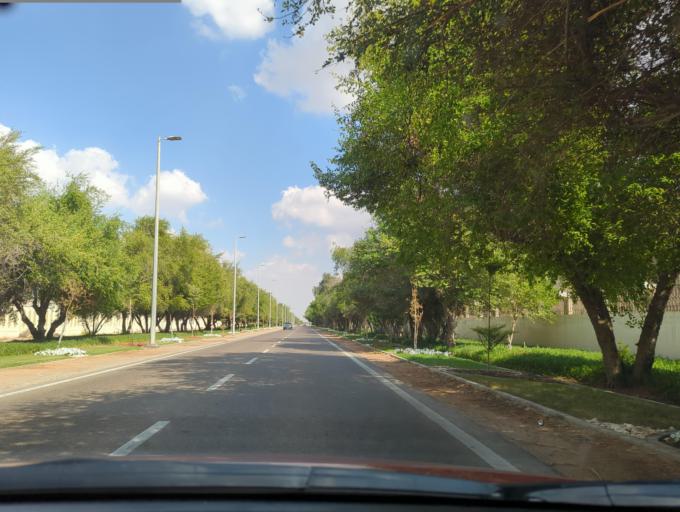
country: AE
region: Abu Dhabi
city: Al Ain
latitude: 24.1694
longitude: 55.6550
